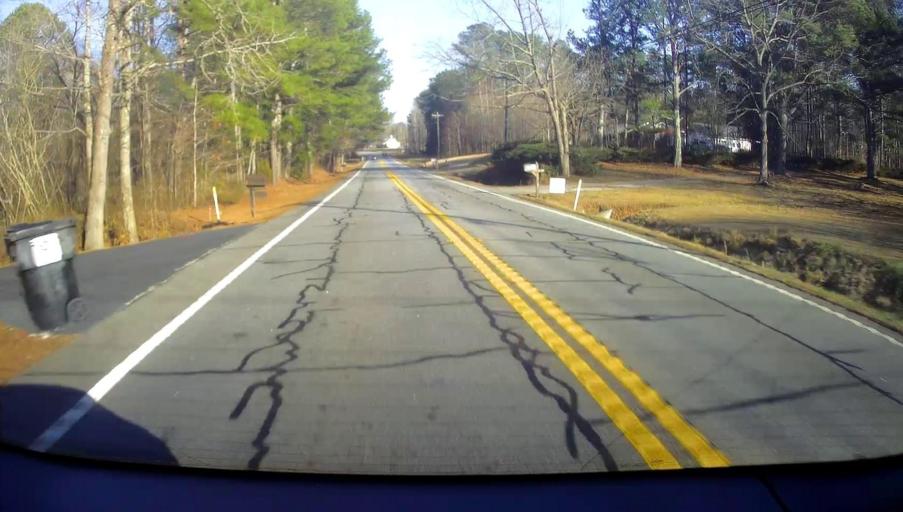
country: US
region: Georgia
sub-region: Henry County
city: Hampton
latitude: 33.4187
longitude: -84.2351
